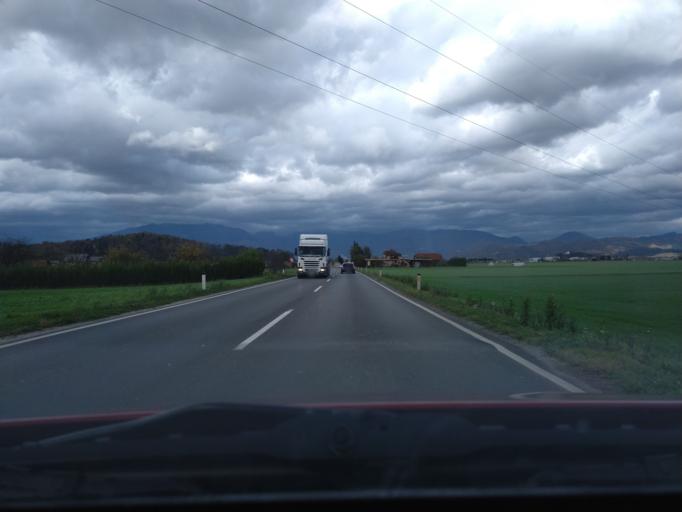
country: SI
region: Trzin
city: Trzin
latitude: 46.1475
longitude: 14.5659
